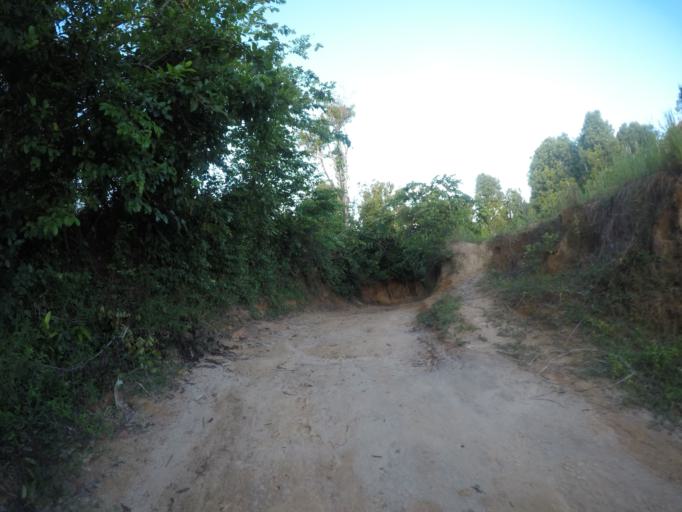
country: TZ
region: Pemba South
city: Mtambile
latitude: -5.3793
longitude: 39.7087
